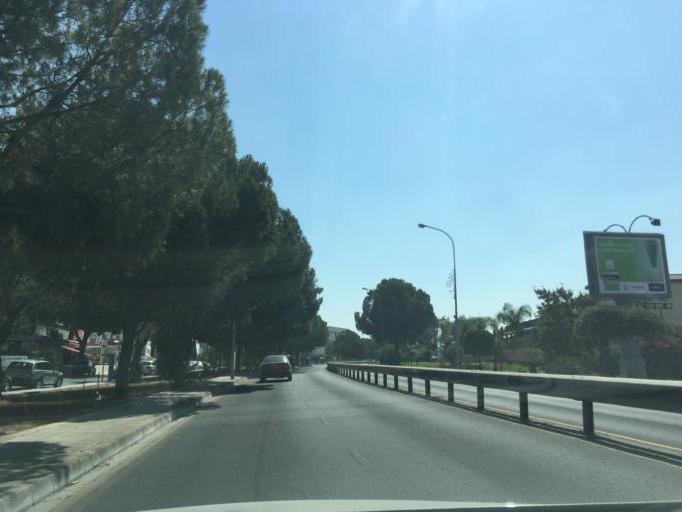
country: CY
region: Lefkosia
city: Nicosia
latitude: 35.1640
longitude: 33.3318
